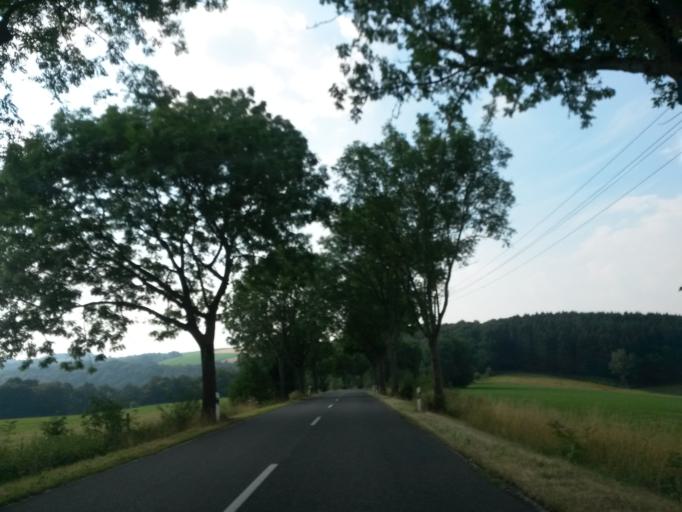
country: DE
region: North Rhine-Westphalia
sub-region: Regierungsbezirk Koln
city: Overath
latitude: 50.9104
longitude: 7.3265
